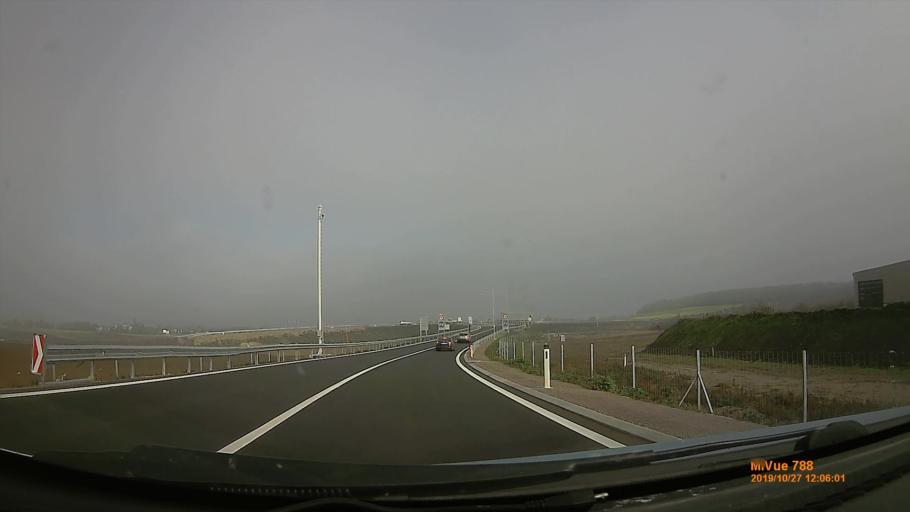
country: AT
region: Lower Austria
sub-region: Politischer Bezirk Mistelbach
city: Drasenhofen
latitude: 48.7699
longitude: 16.6403
